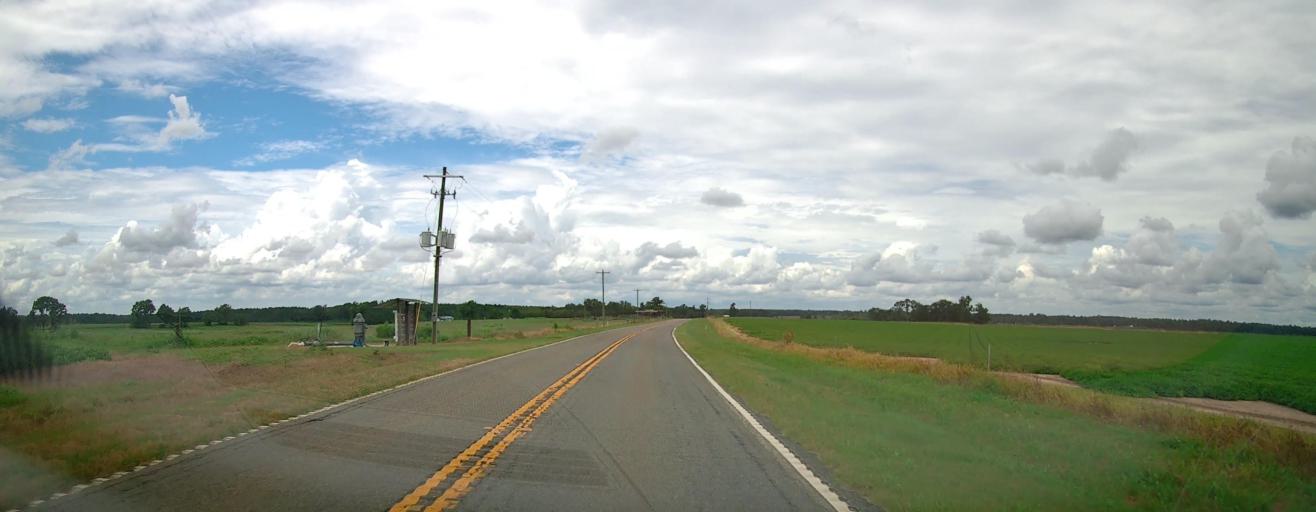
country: US
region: Georgia
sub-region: Dooly County
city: Unadilla
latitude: 32.2668
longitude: -83.8127
